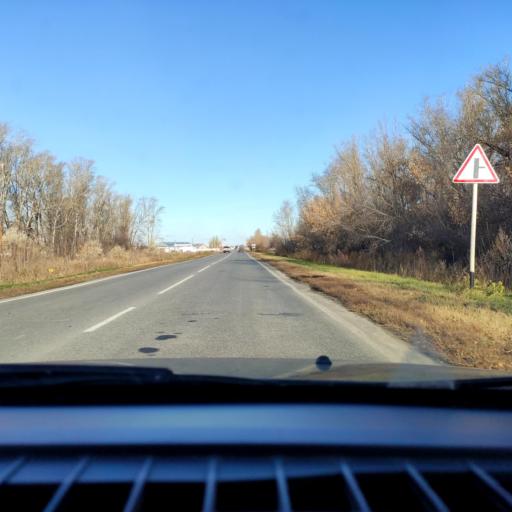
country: RU
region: Samara
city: Tol'yatti
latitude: 53.6301
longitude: 49.3034
